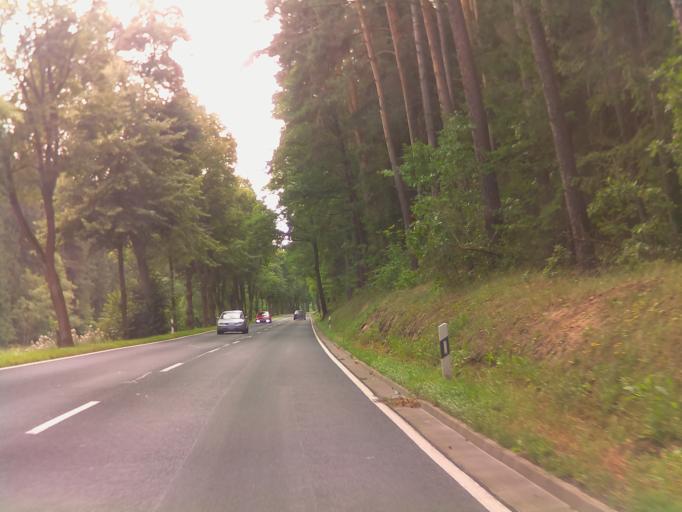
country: DE
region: Thuringia
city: Behringen
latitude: 50.7247
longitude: 10.9932
